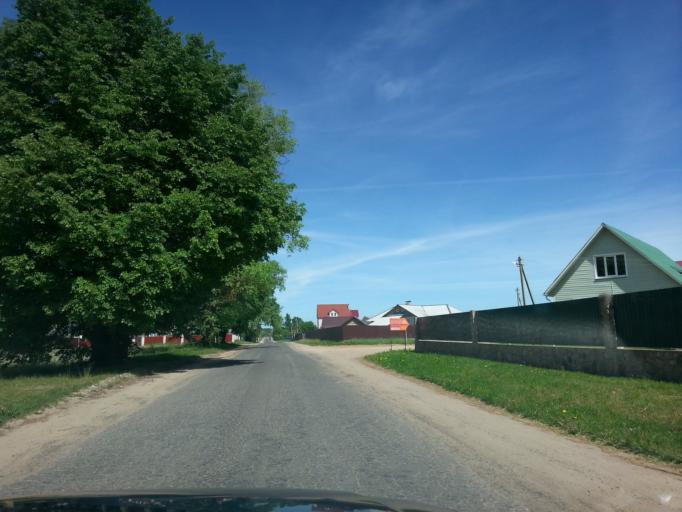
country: BY
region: Minsk
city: Narach
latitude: 54.9242
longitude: 26.6923
